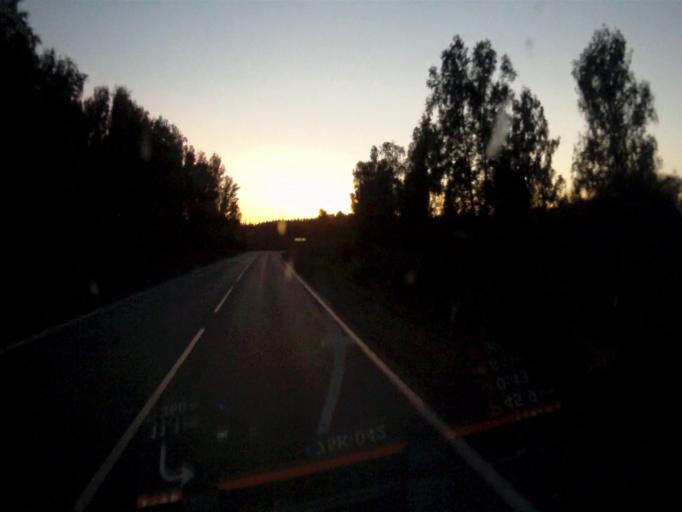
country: RU
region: Chelyabinsk
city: Timiryazevskiy
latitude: 55.2050
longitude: 60.7640
